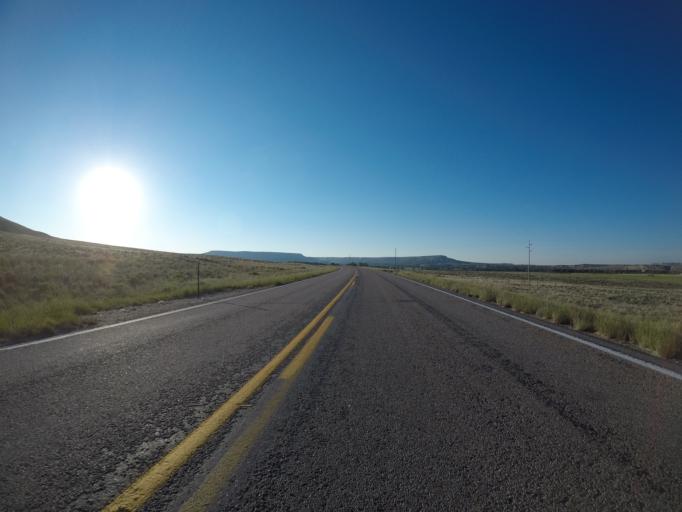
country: US
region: Wyoming
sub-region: Sublette County
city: Marbleton
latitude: 42.5730
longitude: -109.9764
